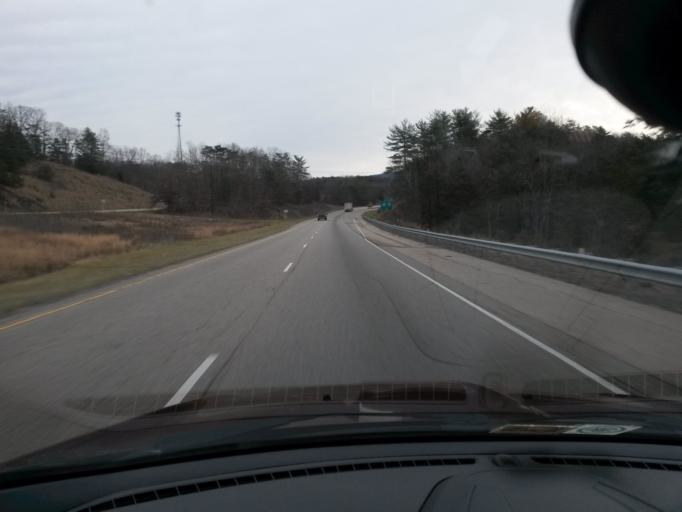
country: US
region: Virginia
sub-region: Alleghany County
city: Clifton Forge
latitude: 37.8305
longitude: -79.7699
